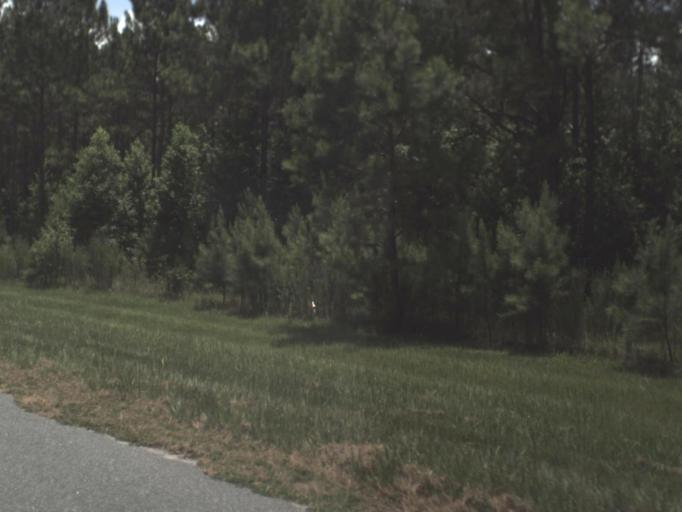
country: US
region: Florida
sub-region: Union County
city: Lake Butler
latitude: 30.0022
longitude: -82.5153
